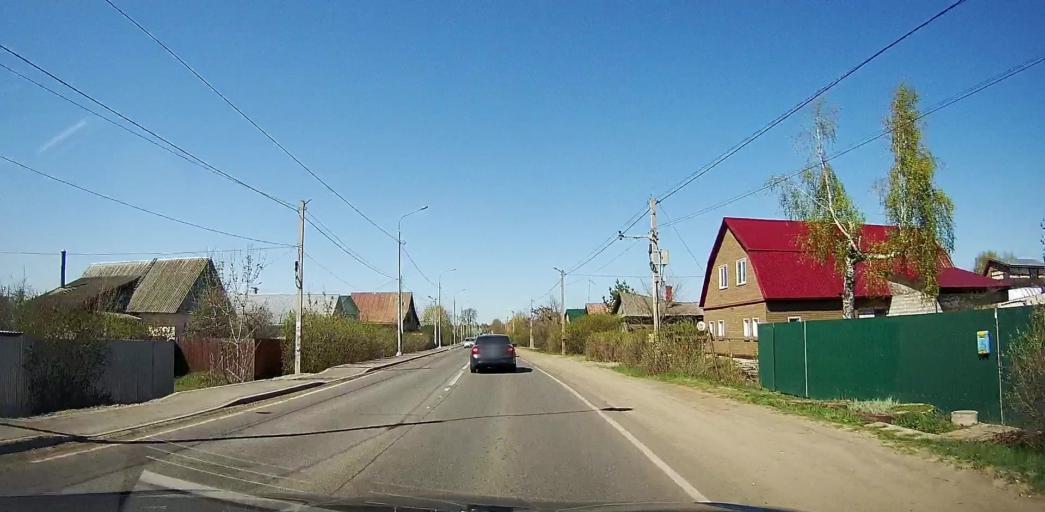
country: RU
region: Moskovskaya
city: Beloozerskiy
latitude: 55.4741
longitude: 38.4111
